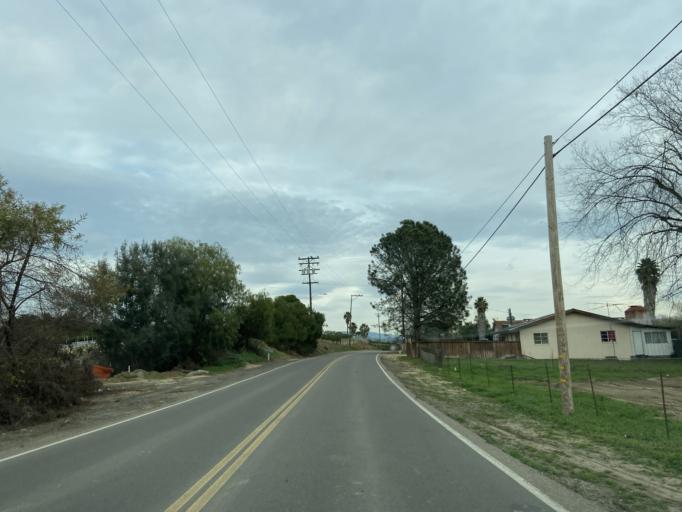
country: US
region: California
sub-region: San Diego County
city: Bonsall
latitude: 33.2592
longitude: -117.2730
